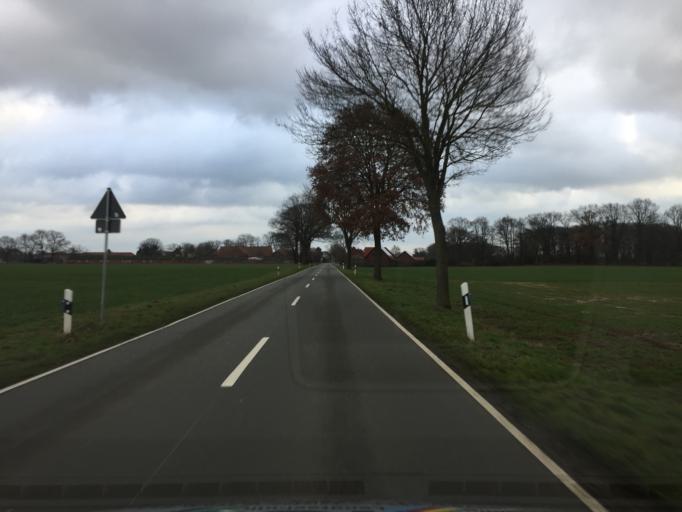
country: DE
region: Lower Saxony
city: Stolzenau
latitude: 52.5296
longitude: 9.0340
